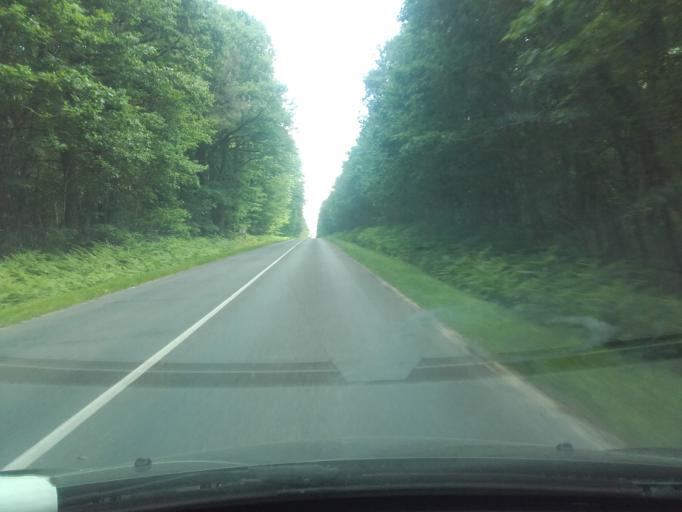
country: FR
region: Centre
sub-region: Departement d'Indre-et-Loire
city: Mazieres-de-Touraine
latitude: 47.3771
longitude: 0.4275
